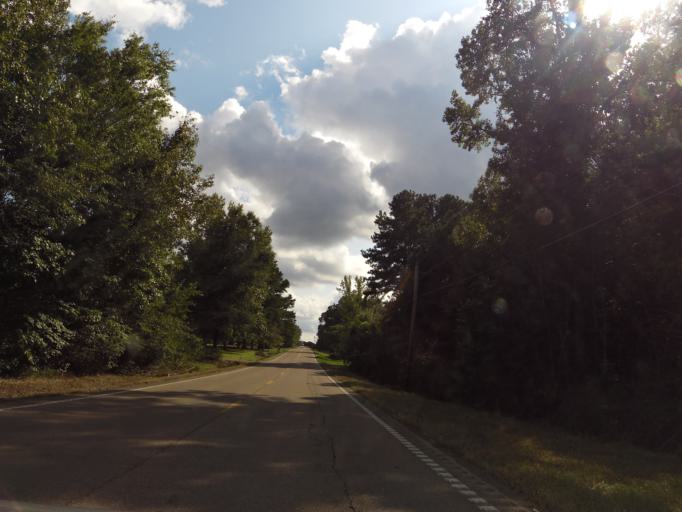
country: US
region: Mississippi
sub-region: Alcorn County
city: Farmington
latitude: 35.0297
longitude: -88.4506
